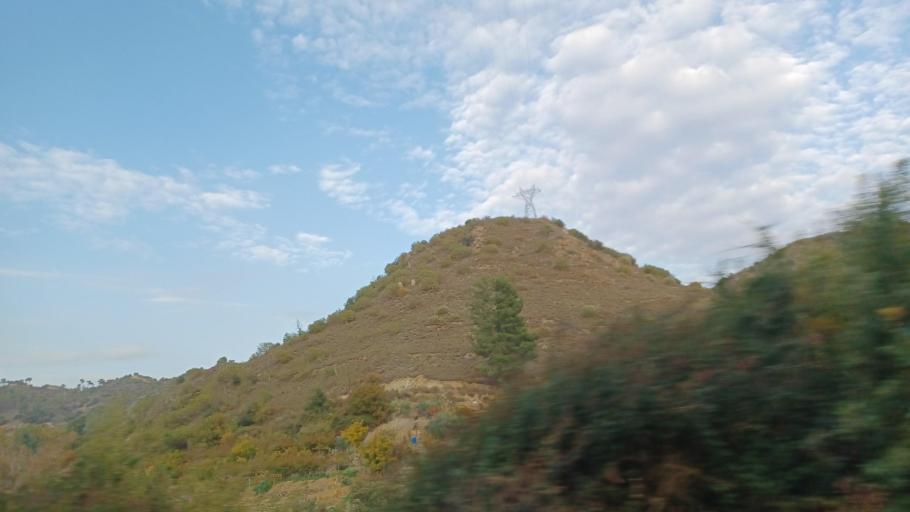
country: CY
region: Limassol
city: Pelendri
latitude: 34.8948
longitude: 32.9358
